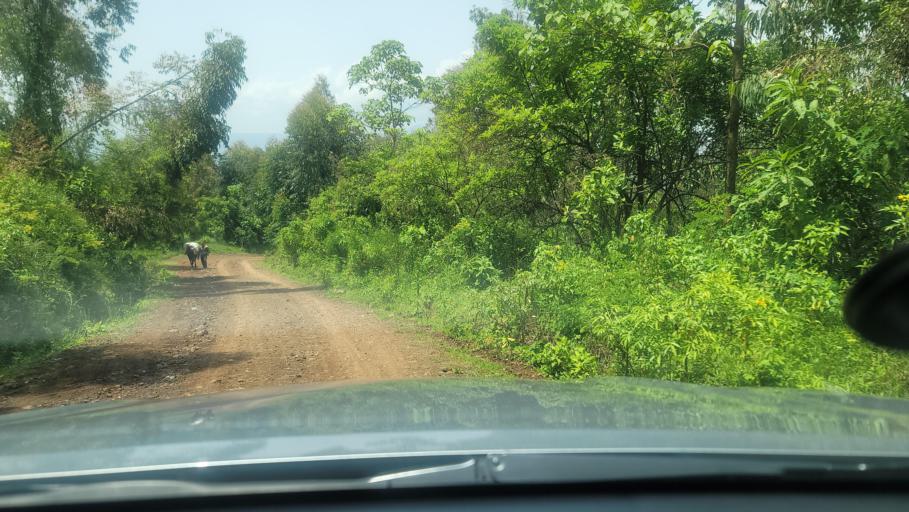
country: ET
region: Oromiya
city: Agaro
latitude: 7.8117
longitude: 36.4113
